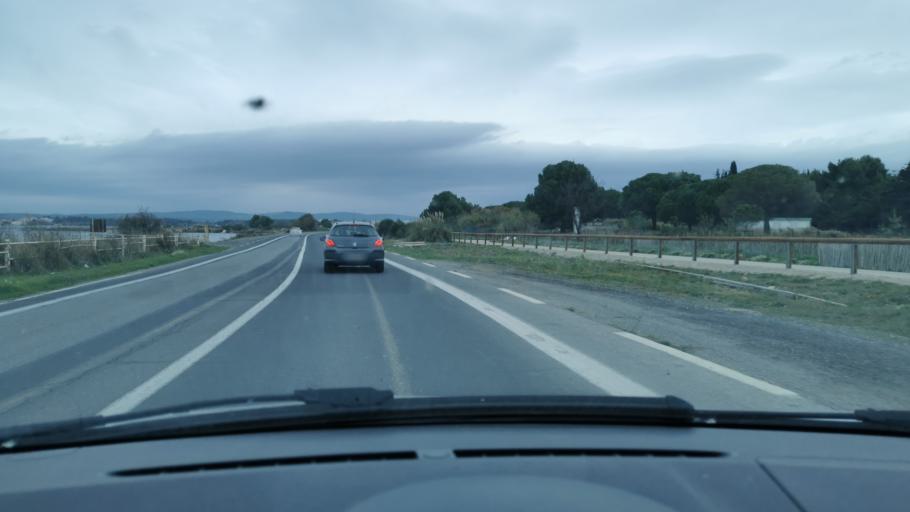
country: FR
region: Languedoc-Roussillon
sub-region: Departement de l'Herault
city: Balaruc-les-Bains
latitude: 43.4308
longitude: 3.7046
